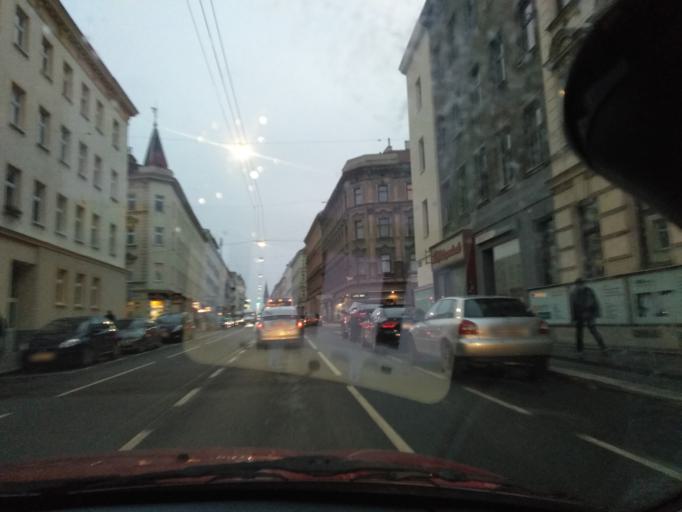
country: AT
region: Vienna
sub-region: Wien Stadt
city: Vienna
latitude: 48.2211
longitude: 16.3211
